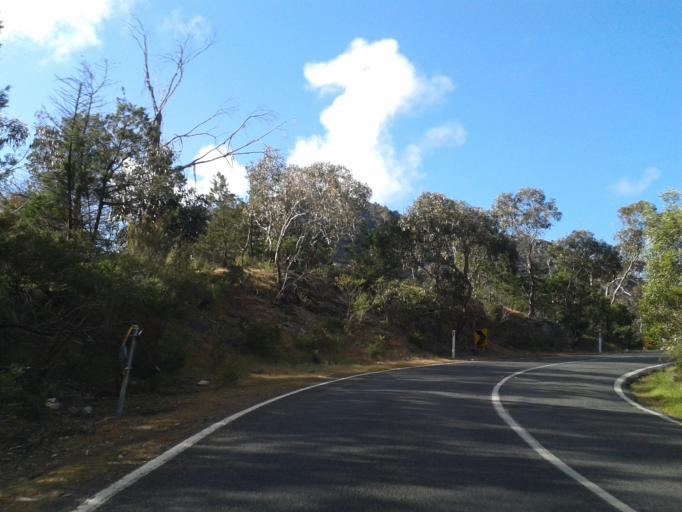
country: AU
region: Victoria
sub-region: Northern Grampians
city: Stawell
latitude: -37.1367
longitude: 142.5093
